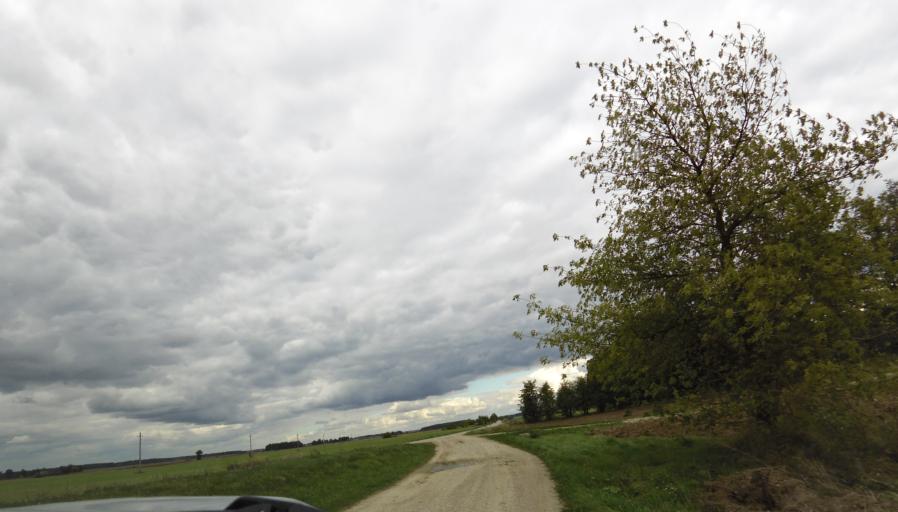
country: LT
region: Panevezys
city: Pasvalys
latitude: 56.0624
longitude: 24.2780
